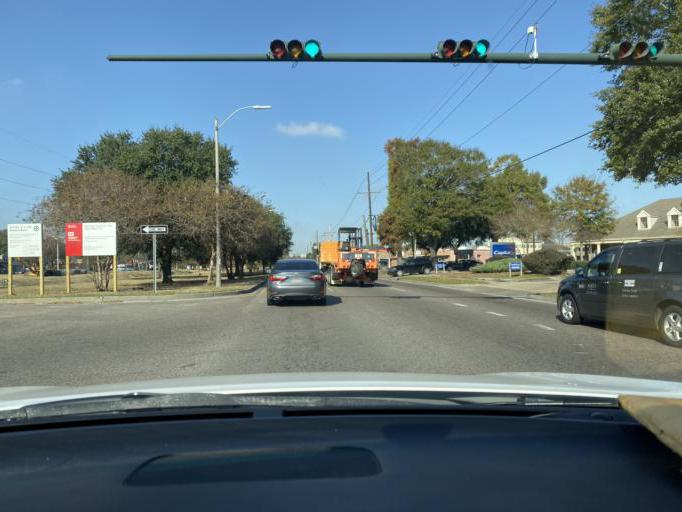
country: US
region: Louisiana
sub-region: Jefferson Parish
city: Terrytown
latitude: 29.9230
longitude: -90.0171
